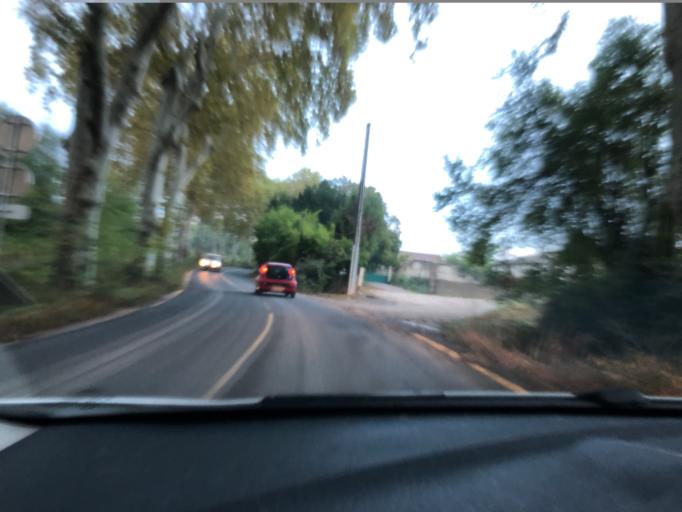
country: FR
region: Languedoc-Roussillon
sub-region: Departement de l'Herault
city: Montferrier-sur-Lez
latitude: 43.6616
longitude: 3.8629
